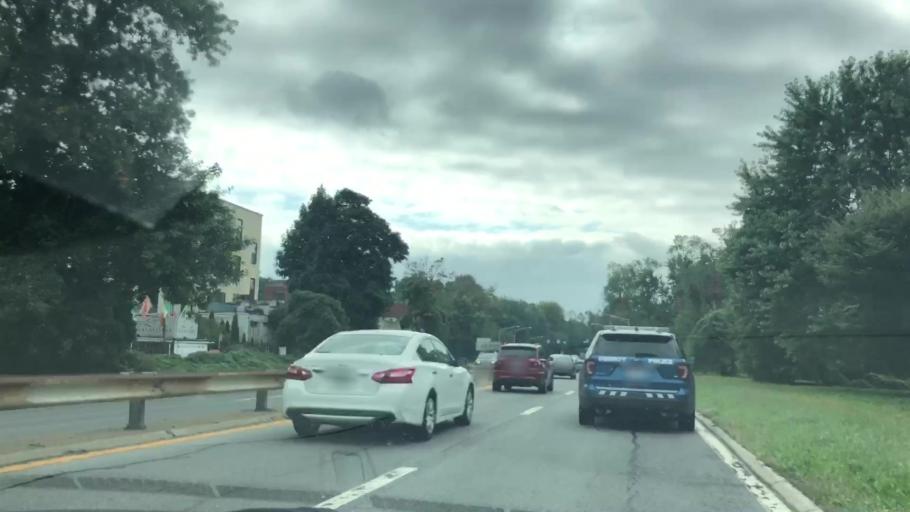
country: US
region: New York
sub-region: Westchester County
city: Hastings-on-Hudson
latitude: 40.9763
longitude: -73.8686
